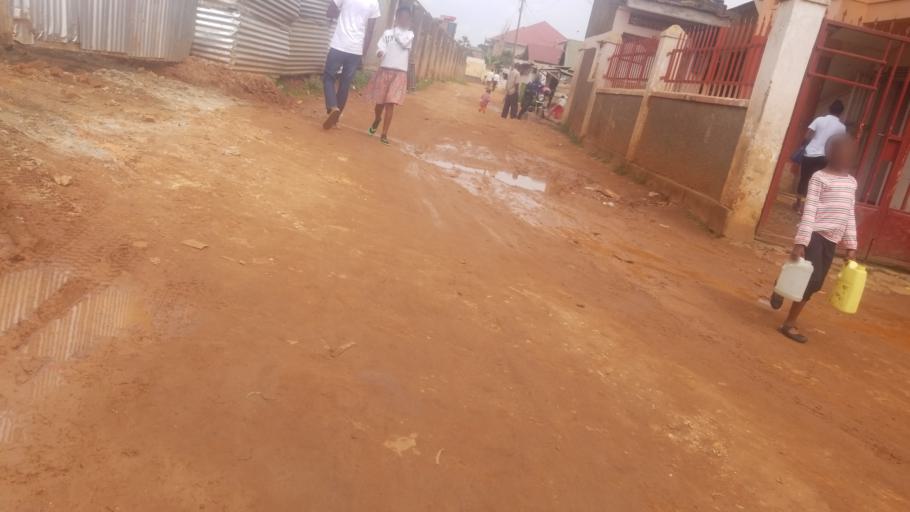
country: UG
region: Central Region
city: Kampala Central Division
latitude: 0.3323
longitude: 32.5611
